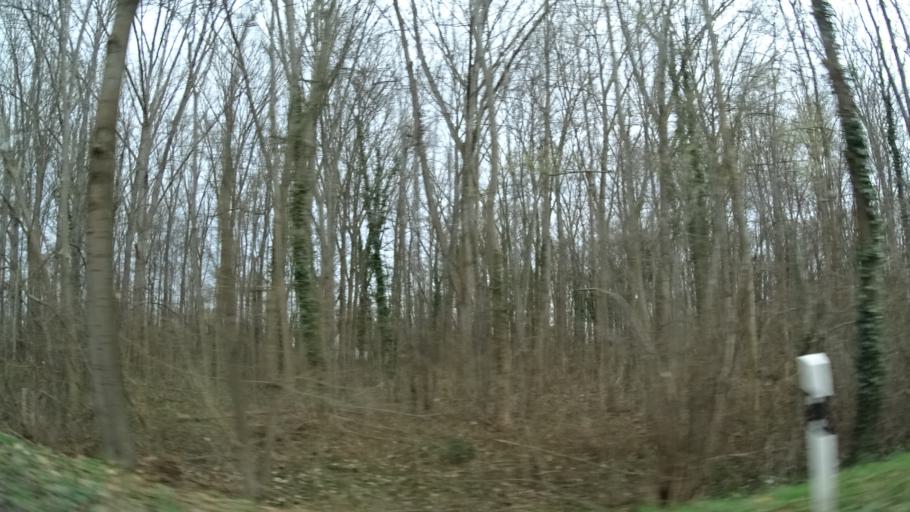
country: DE
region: Rheinland-Pfalz
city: Worms
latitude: 49.6342
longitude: 8.3876
